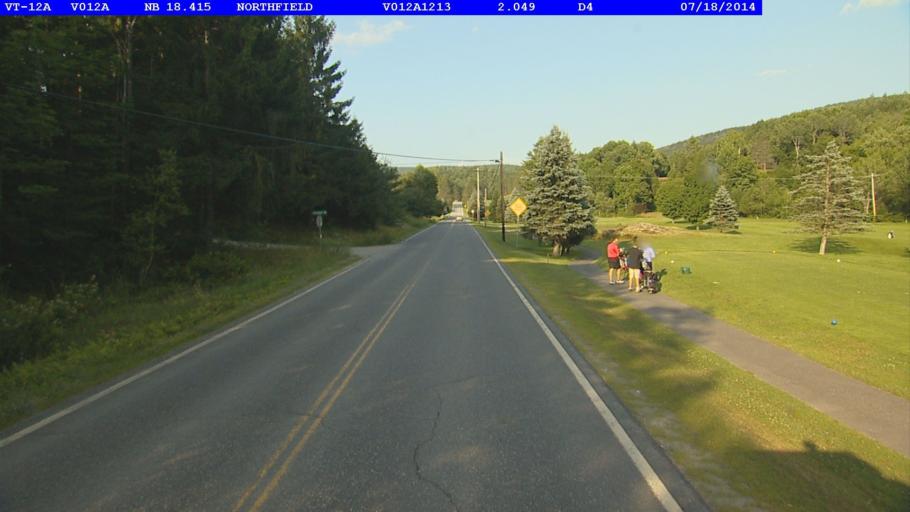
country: US
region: Vermont
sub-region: Washington County
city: Northfield
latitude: 44.1110
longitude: -72.6892
